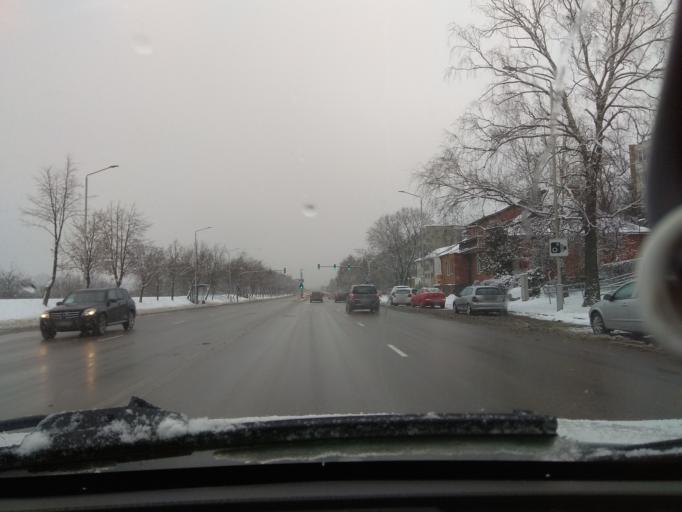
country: LT
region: Kauno apskritis
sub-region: Kaunas
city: Kaunas
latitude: 54.9179
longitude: 23.9126
